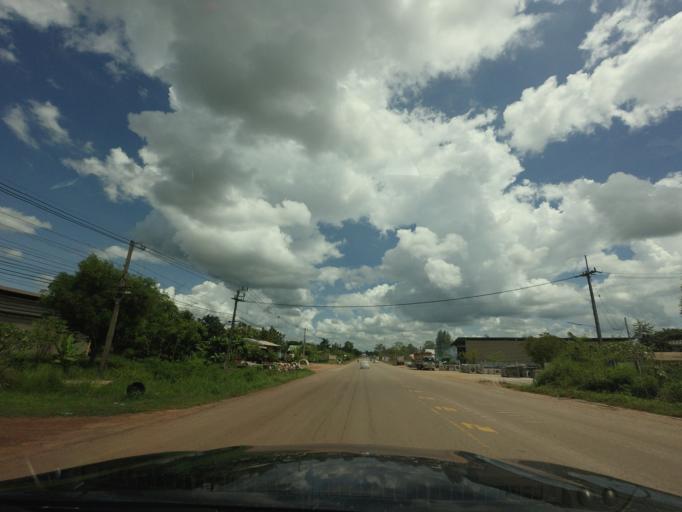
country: TH
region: Changwat Udon Thani
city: Ban Dung
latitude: 17.6790
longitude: 103.2388
